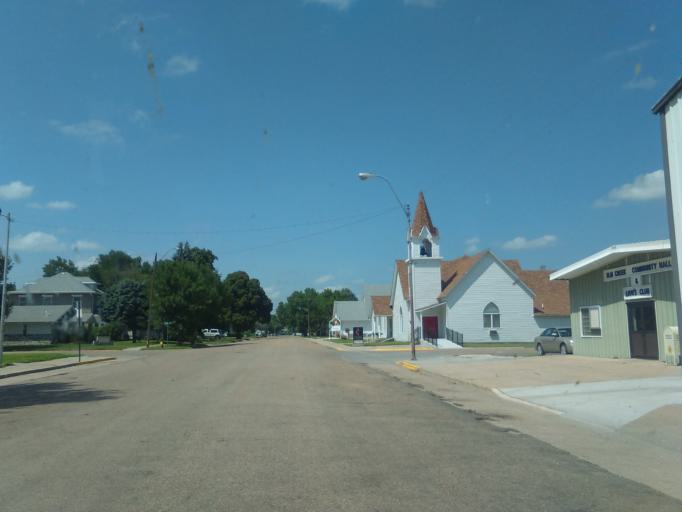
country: US
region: Nebraska
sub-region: Phelps County
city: Holdrege
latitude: 40.7190
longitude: -99.3732
